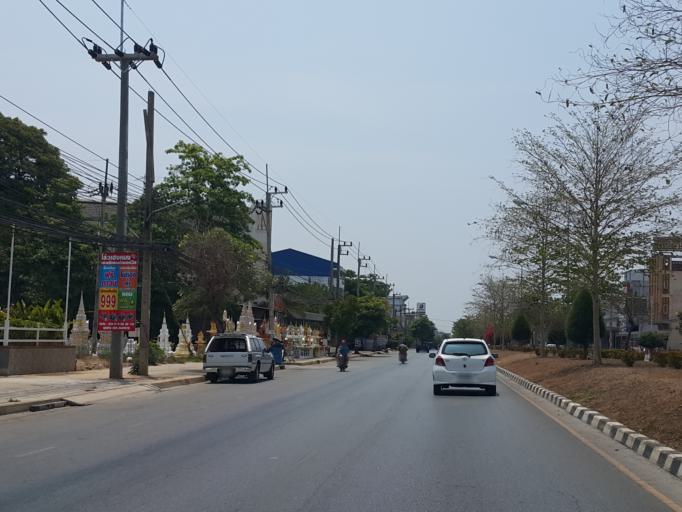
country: TH
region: Kanchanaburi
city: Kanchanaburi
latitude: 14.0411
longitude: 99.5155
